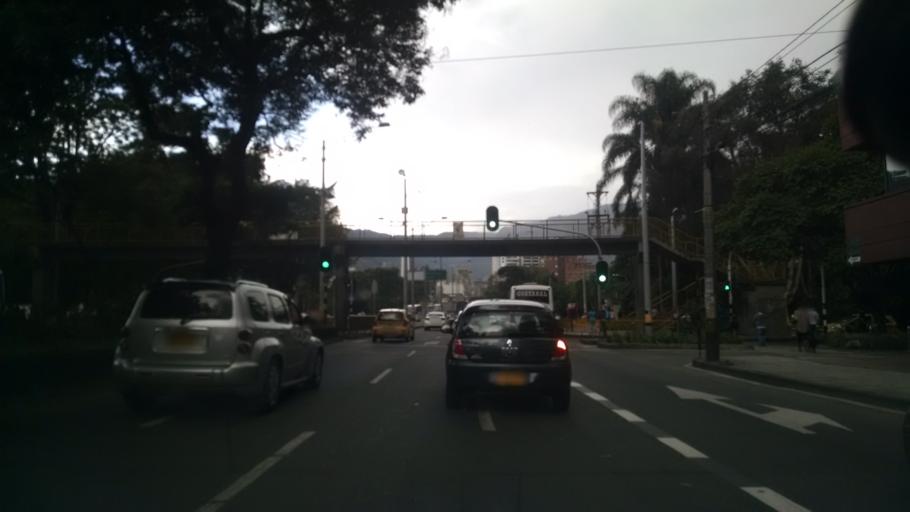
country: CO
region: Antioquia
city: Medellin
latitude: 6.2554
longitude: -75.5797
